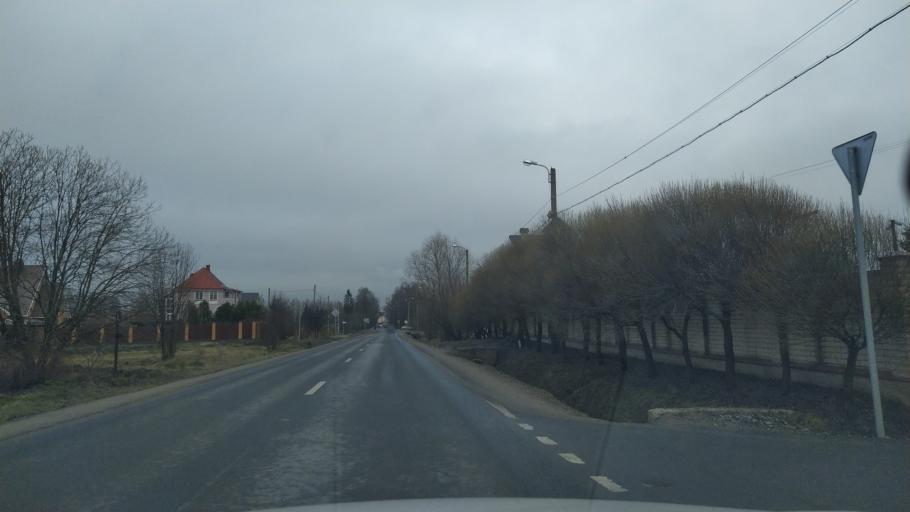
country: RU
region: St.-Petersburg
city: Aleksandrovskaya
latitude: 59.7244
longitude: 30.3493
